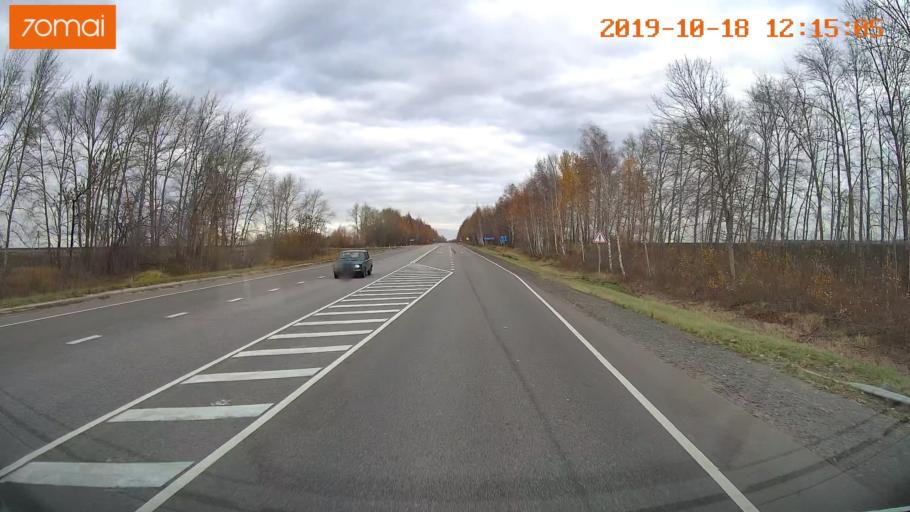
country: RU
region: Rjazan
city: Zakharovo
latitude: 54.4391
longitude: 39.3942
